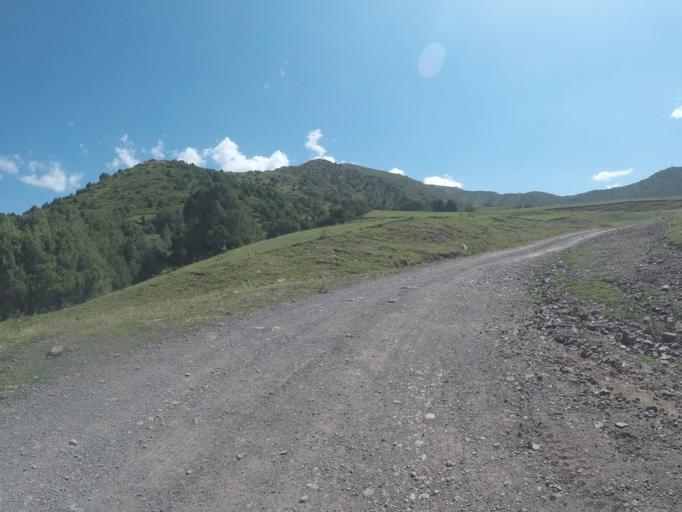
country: KG
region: Chuy
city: Bishkek
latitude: 42.6474
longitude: 74.5588
